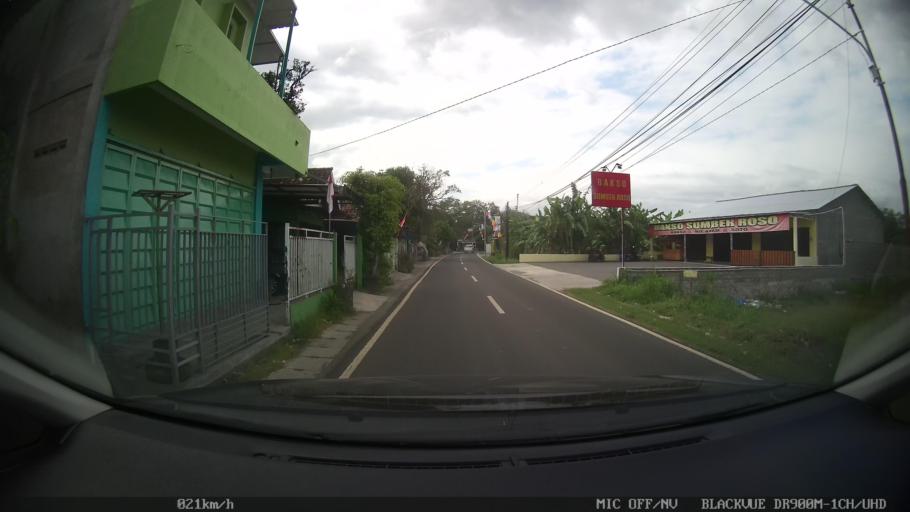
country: ID
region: Daerah Istimewa Yogyakarta
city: Depok
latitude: -7.8063
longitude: 110.4547
